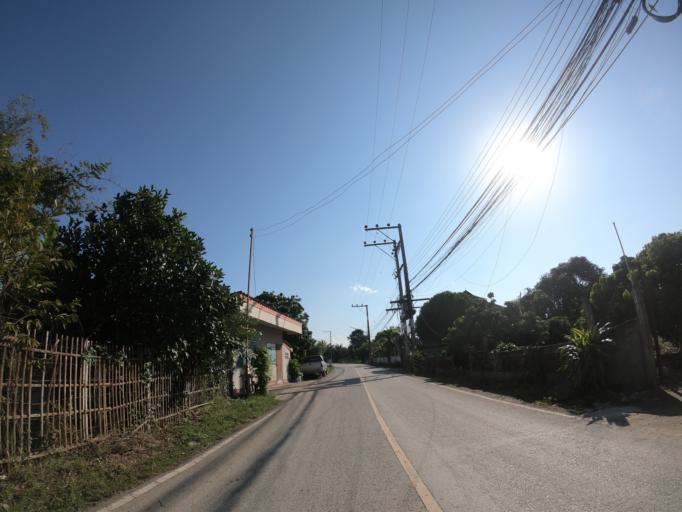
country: TH
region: Chiang Mai
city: Saraphi
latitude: 18.7011
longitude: 98.9891
